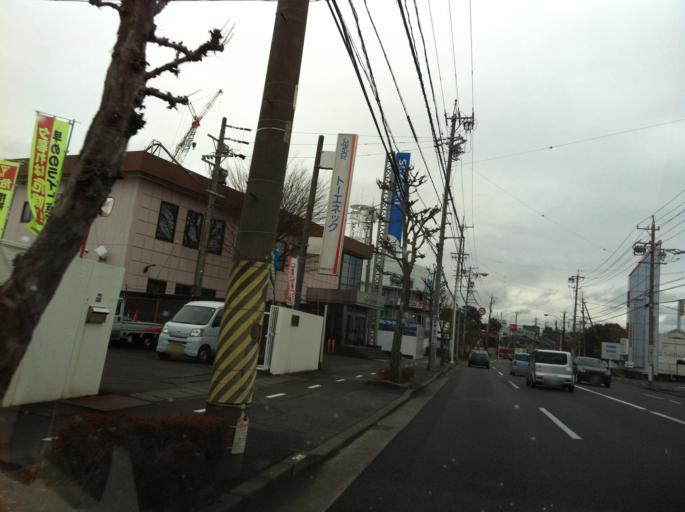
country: JP
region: Shizuoka
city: Shizuoka-shi
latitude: 34.9874
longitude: 138.4242
